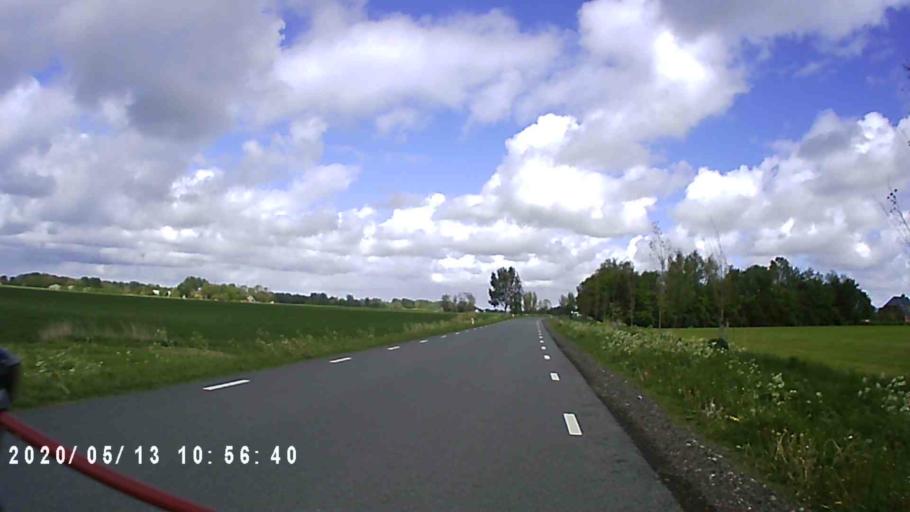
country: NL
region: Groningen
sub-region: Gemeente Zuidhorn
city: Grijpskerk
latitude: 53.2707
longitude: 6.3353
